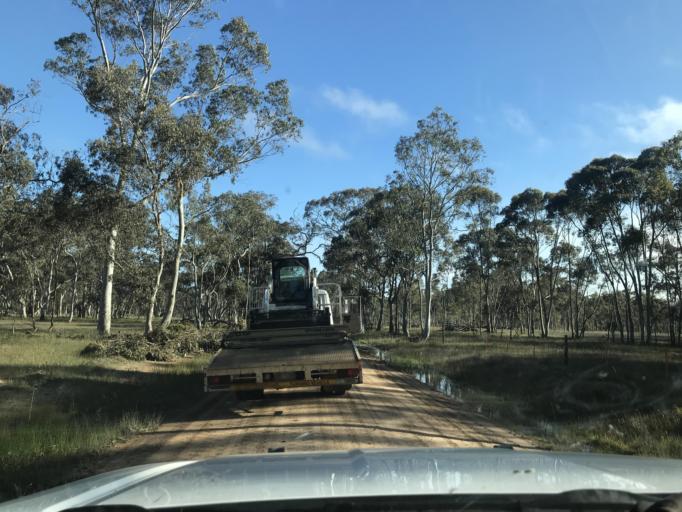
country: AU
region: South Australia
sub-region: Wattle Range
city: Penola
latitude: -37.1621
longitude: 141.1771
